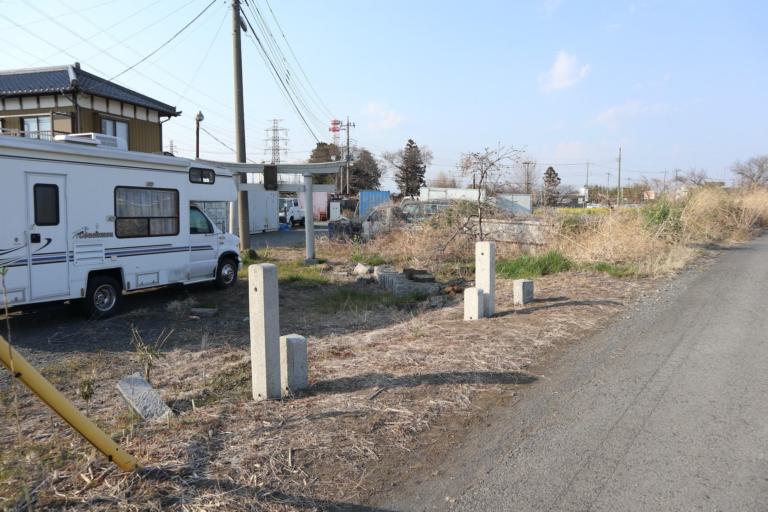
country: JP
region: Gunma
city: Tatebayashi
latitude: 36.2772
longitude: 139.5570
